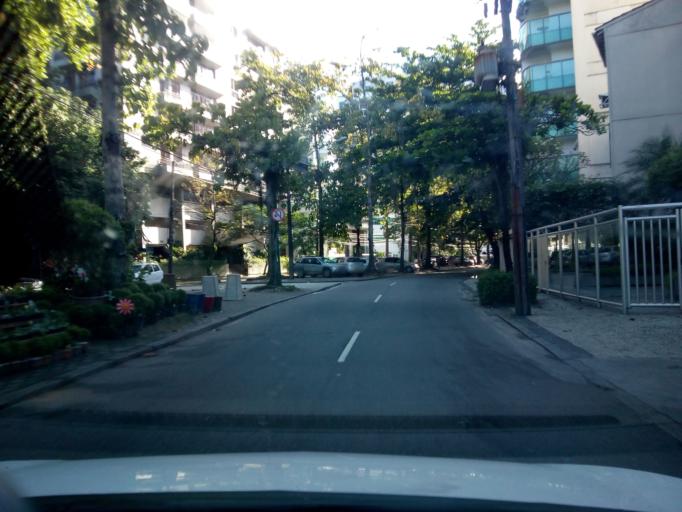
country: BR
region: Rio de Janeiro
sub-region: Rio De Janeiro
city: Rio de Janeiro
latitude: -22.9623
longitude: -43.2117
